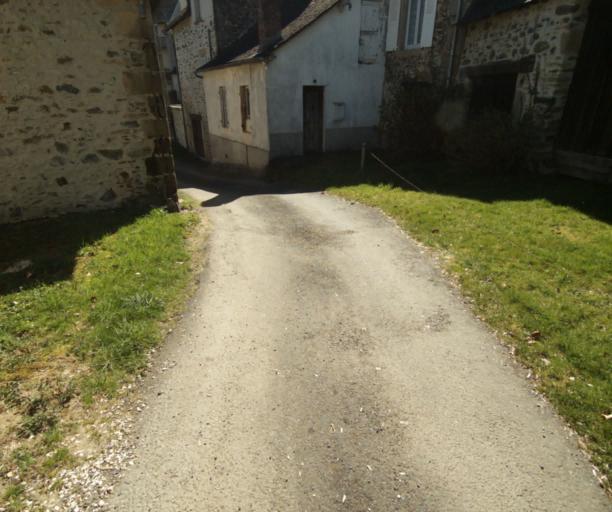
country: FR
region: Limousin
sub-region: Departement de la Correze
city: Chamboulive
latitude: 45.4329
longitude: 1.7032
